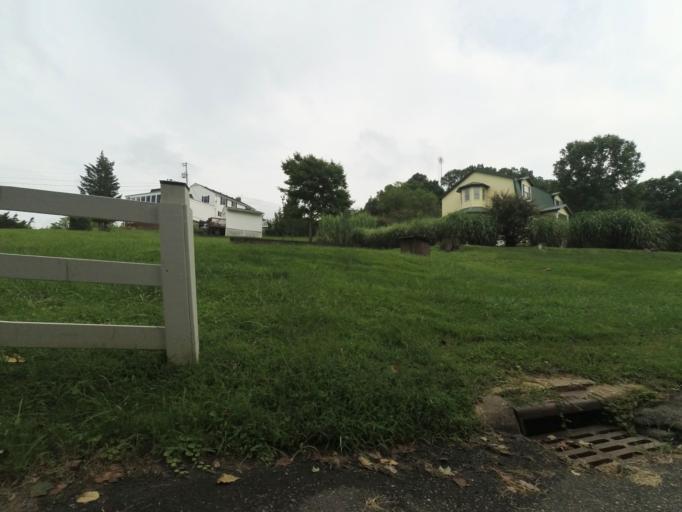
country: US
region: West Virginia
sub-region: Cabell County
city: Huntington
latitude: 38.3994
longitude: -82.4367
